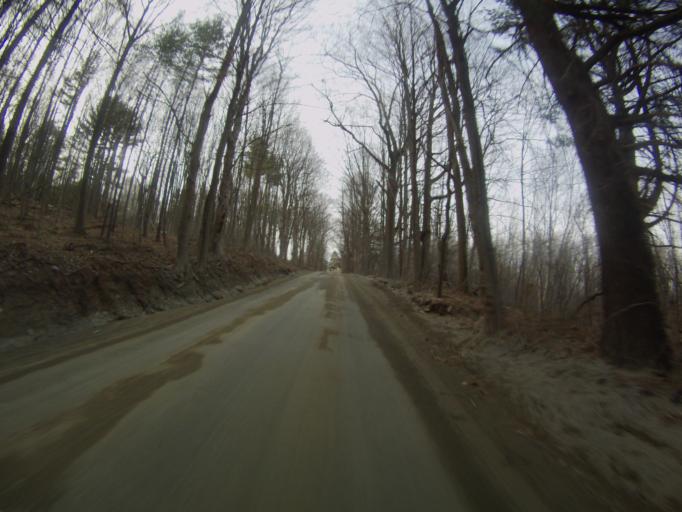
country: US
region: Vermont
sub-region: Addison County
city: Middlebury (village)
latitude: 44.0237
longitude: -73.2591
